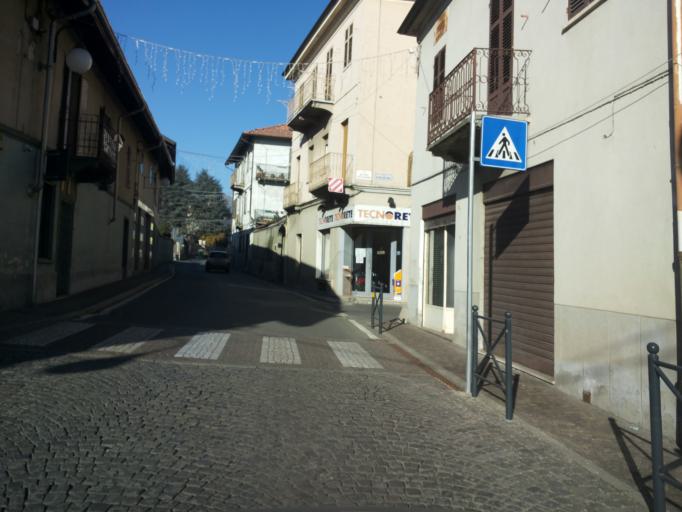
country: IT
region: Piedmont
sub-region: Provincia di Biella
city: Ponderano
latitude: 45.5382
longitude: 8.0548
